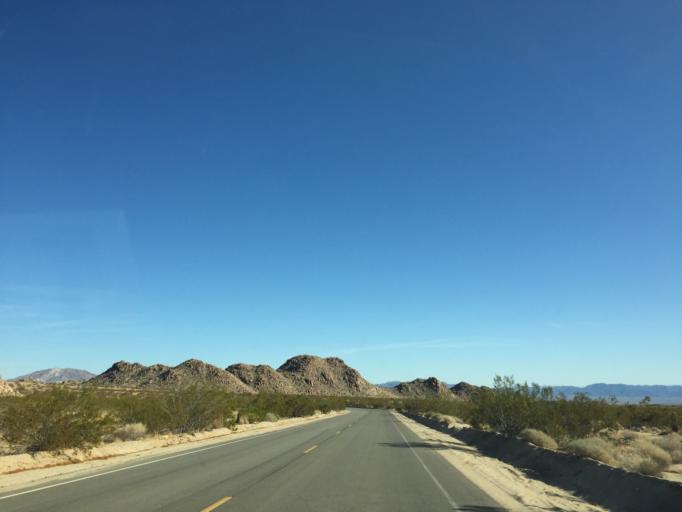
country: US
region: California
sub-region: Riverside County
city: Mecca
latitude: 33.8262
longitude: -115.7598
